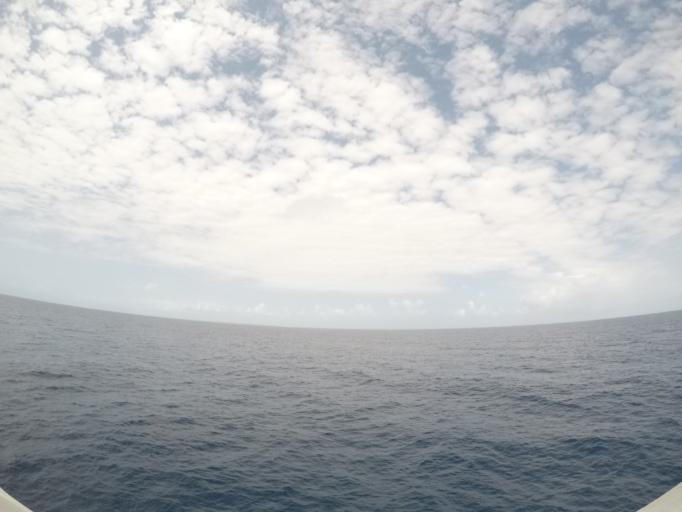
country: TZ
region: Zanzibar North
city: Nungwi
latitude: -5.5977
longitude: 39.3437
